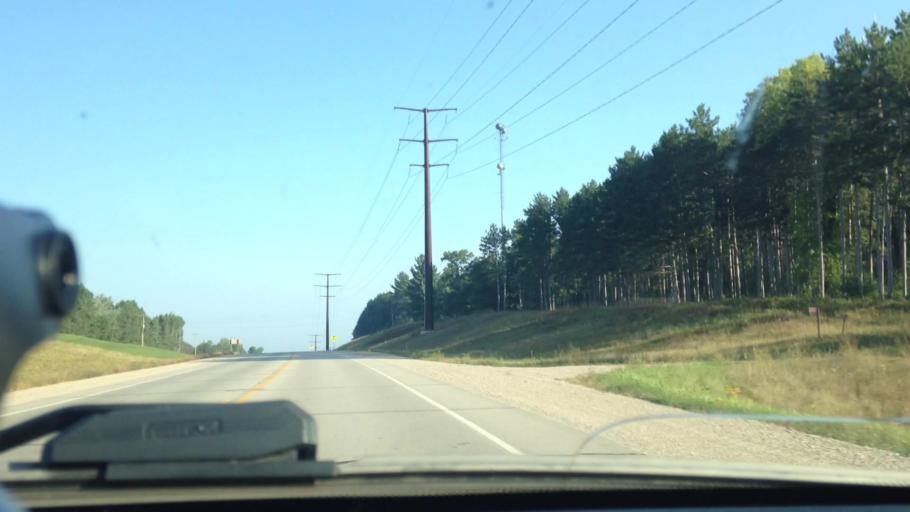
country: US
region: Wisconsin
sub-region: Marinette County
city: Peshtigo
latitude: 45.2111
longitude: -87.9949
